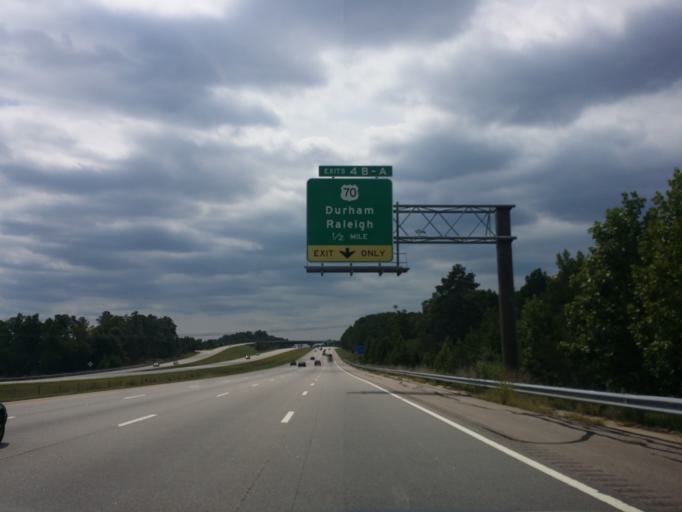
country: US
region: North Carolina
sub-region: Wake County
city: Morrisville
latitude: 35.9095
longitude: -78.7619
